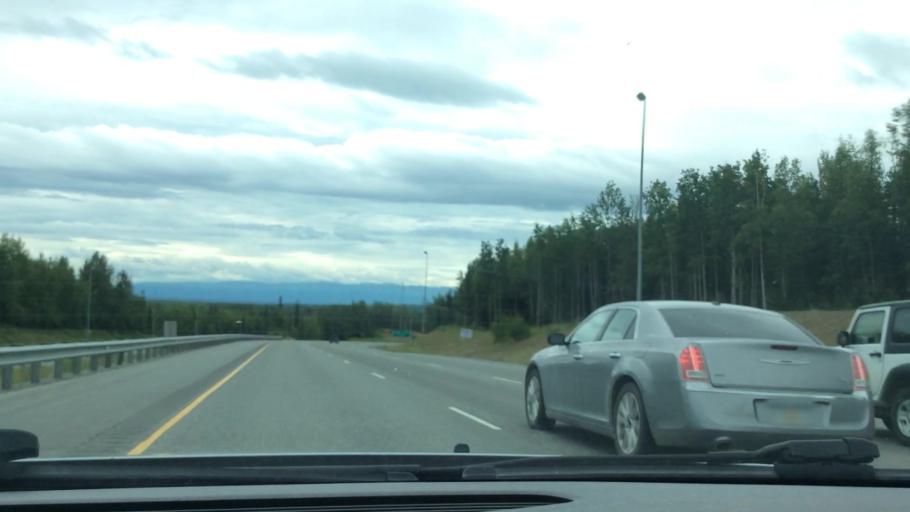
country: US
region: Alaska
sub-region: Anchorage Municipality
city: Eagle River
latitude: 61.3022
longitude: -149.5876
